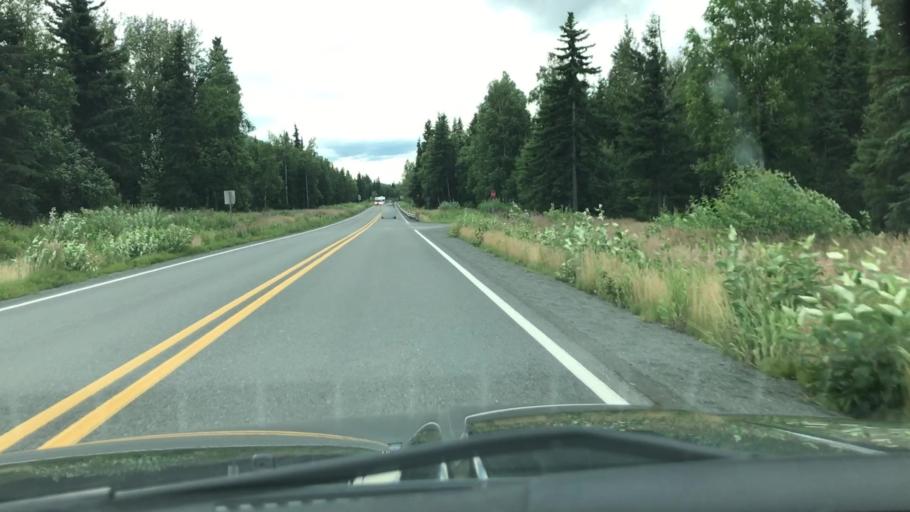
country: US
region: Alaska
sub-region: Kenai Peninsula Borough
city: Seward
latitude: 60.4837
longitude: -149.8901
